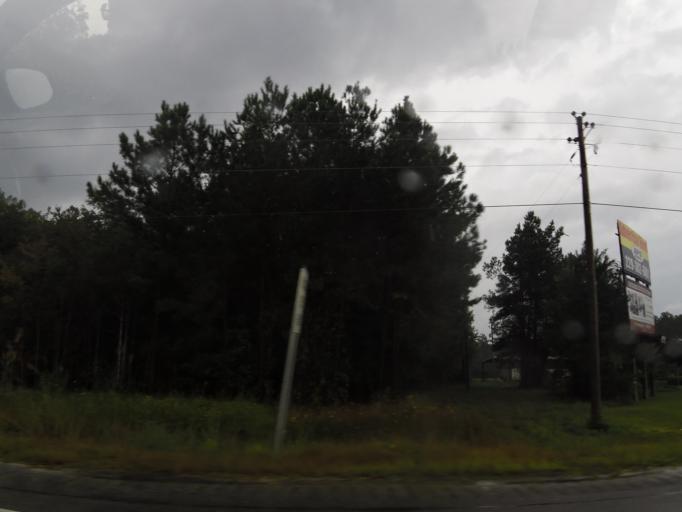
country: US
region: Georgia
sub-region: Wayne County
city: Jesup
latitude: 31.5881
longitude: -81.8622
